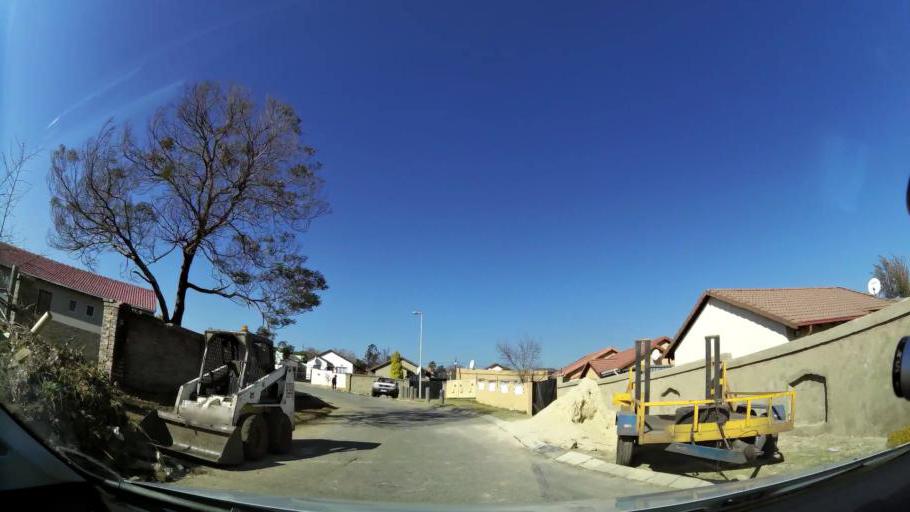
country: ZA
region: Gauteng
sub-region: City of Johannesburg Metropolitan Municipality
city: Modderfontein
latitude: -26.1105
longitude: 28.1272
